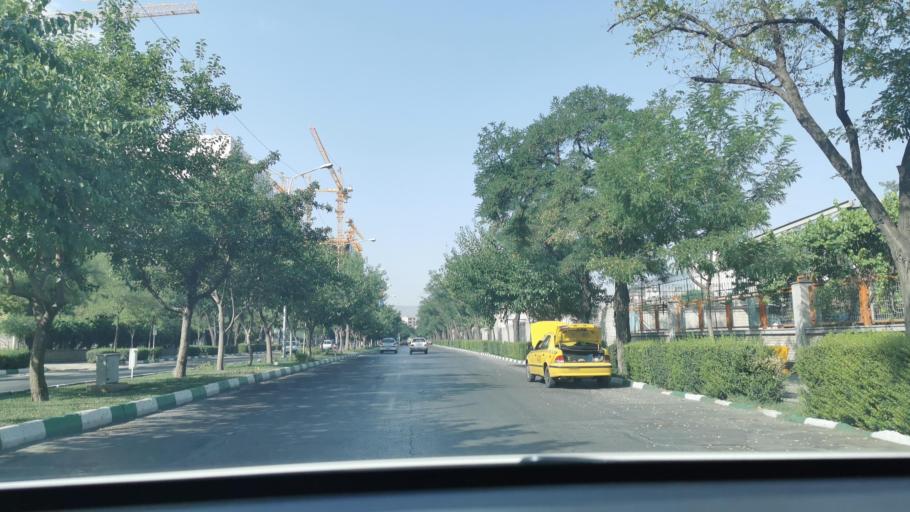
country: IR
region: Razavi Khorasan
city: Mashhad
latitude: 36.3202
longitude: 59.5626
